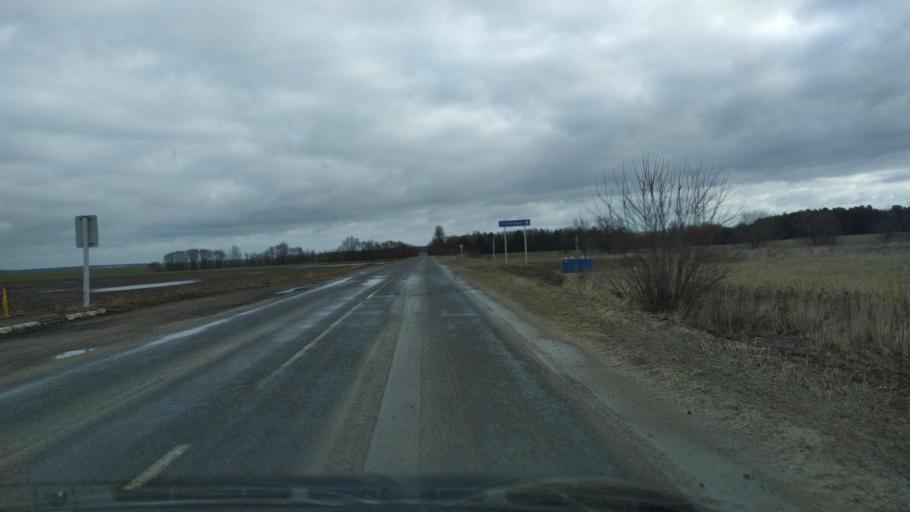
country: BY
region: Brest
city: Kamyanyets
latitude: 52.4277
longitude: 23.8151
